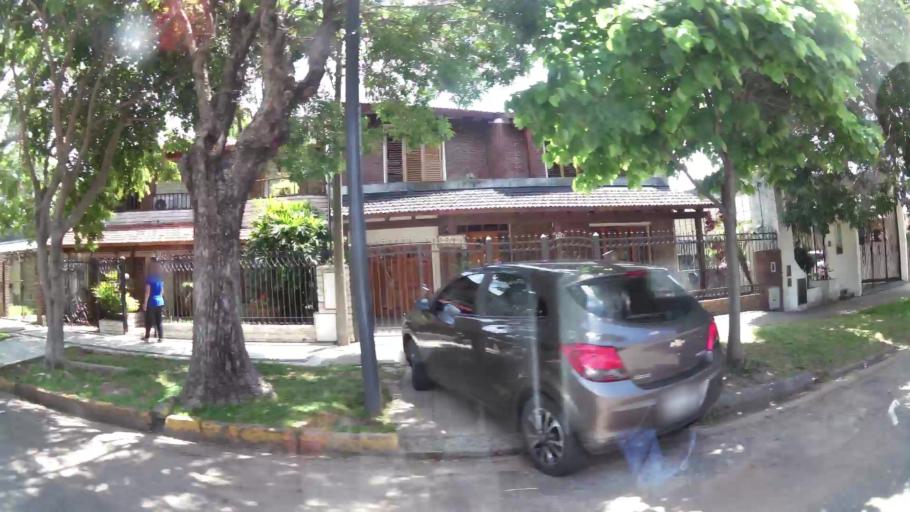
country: AR
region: Santa Fe
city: Gobernador Galvez
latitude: -32.9990
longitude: -60.6245
